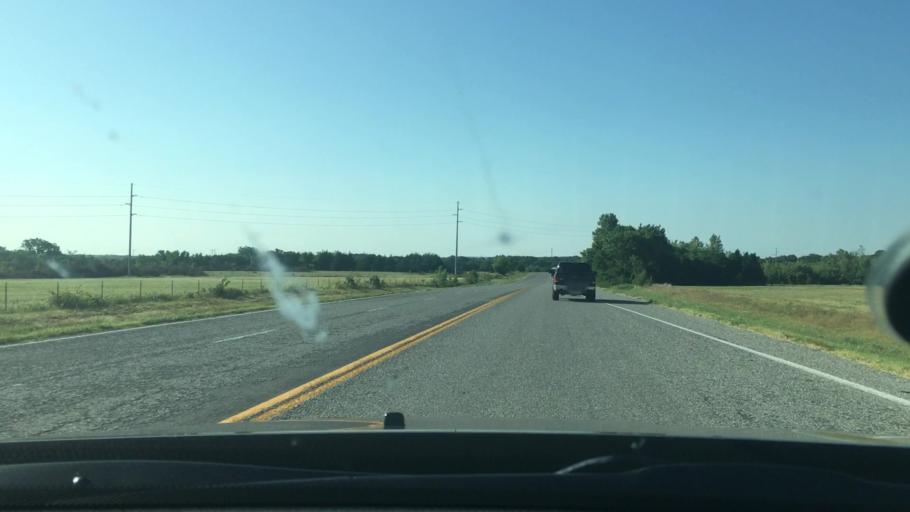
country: US
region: Oklahoma
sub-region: Johnston County
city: Tishomingo
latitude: 34.2766
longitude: -96.7777
